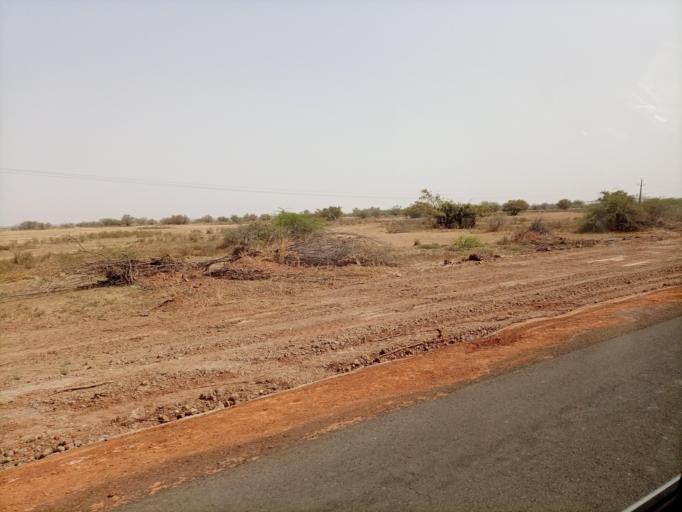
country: SN
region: Fatick
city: Foundiougne
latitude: 14.1629
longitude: -16.4658
